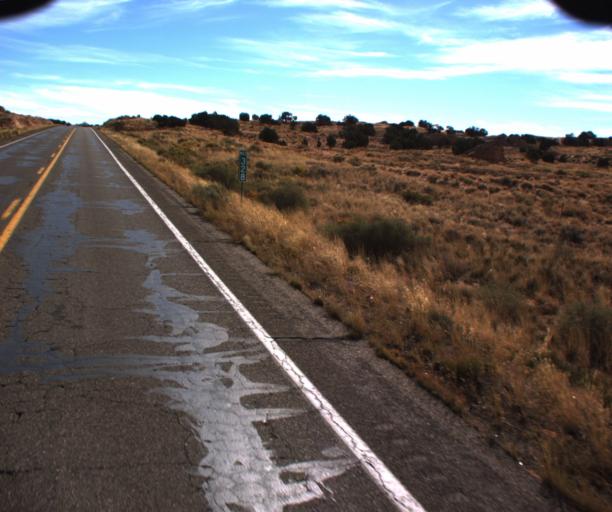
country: US
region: Arizona
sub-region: Coconino County
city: Kaibito
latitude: 36.5799
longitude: -111.1387
